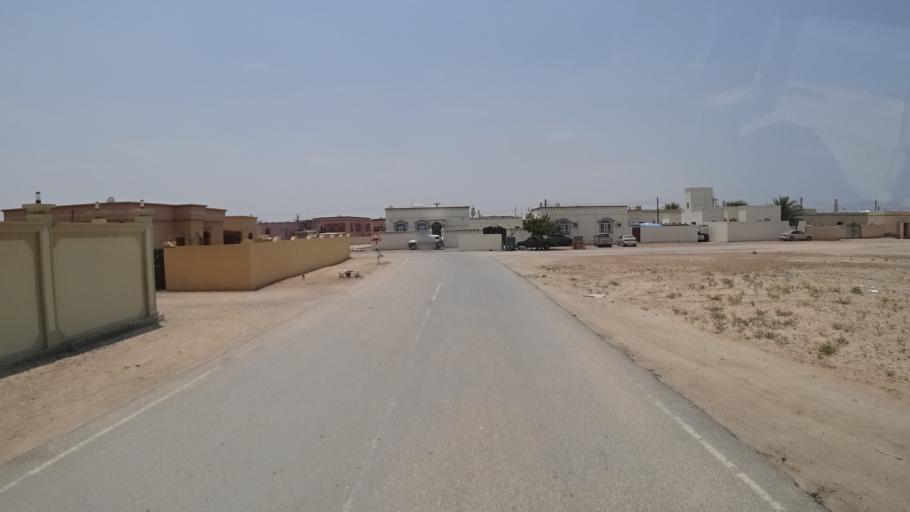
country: OM
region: Ash Sharqiyah
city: Sur
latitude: 22.5213
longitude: 59.7980
